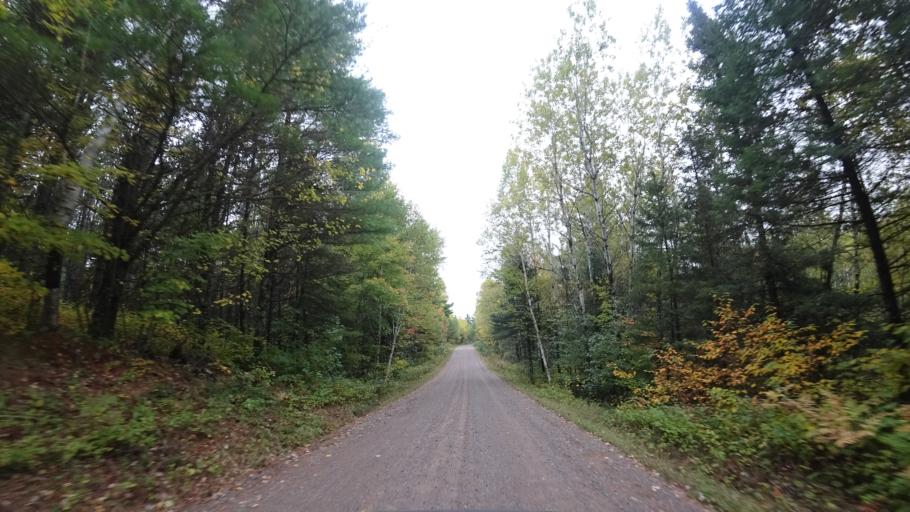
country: US
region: Wisconsin
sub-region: Sawyer County
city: Little Round Lake
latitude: 46.0673
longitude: -90.9943
